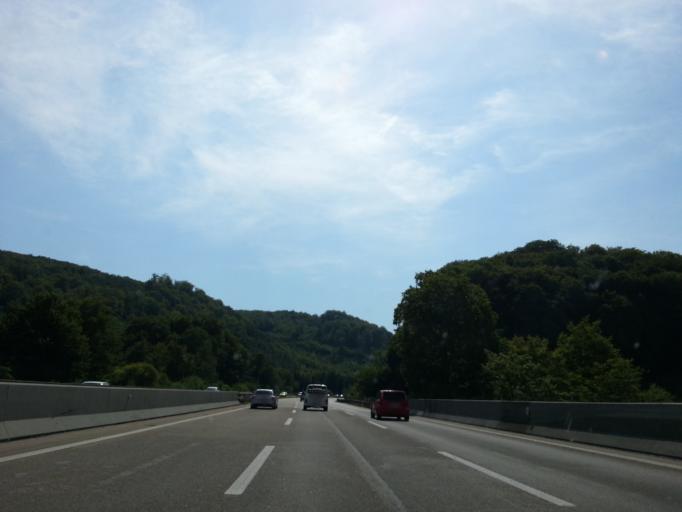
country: CH
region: Basel-Landschaft
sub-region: Bezirk Liestal
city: Arisdorf
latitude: 47.4968
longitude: 7.7663
